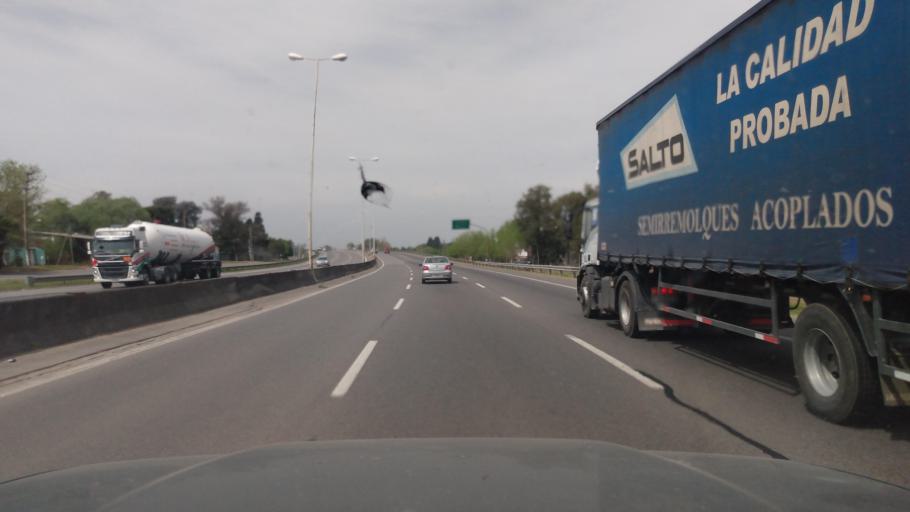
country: AR
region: Buenos Aires
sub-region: Partido de Pilar
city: Pilar
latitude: -34.4279
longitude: -58.9964
